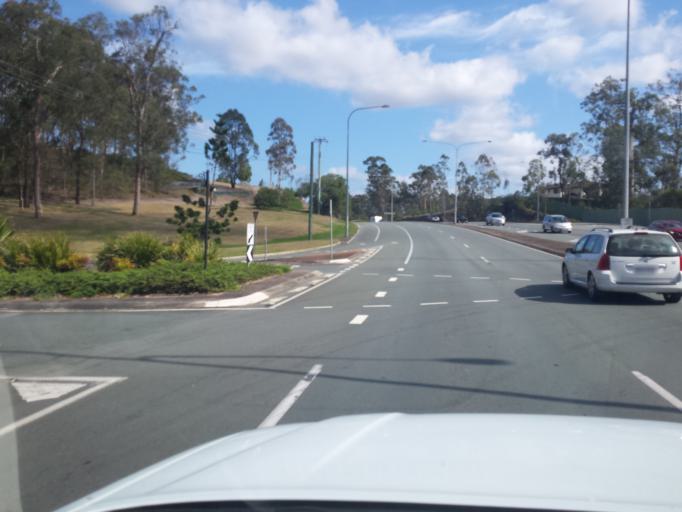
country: AU
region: Queensland
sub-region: Brisbane
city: Bridegman Downs
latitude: -27.3689
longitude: 152.9791
